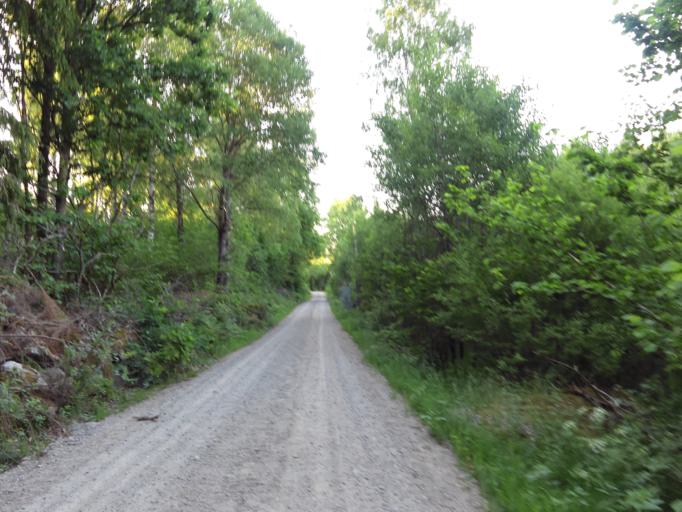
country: SE
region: Blekinge
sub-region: Olofstroms Kommun
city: Olofstroem
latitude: 56.4091
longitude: 14.5605
